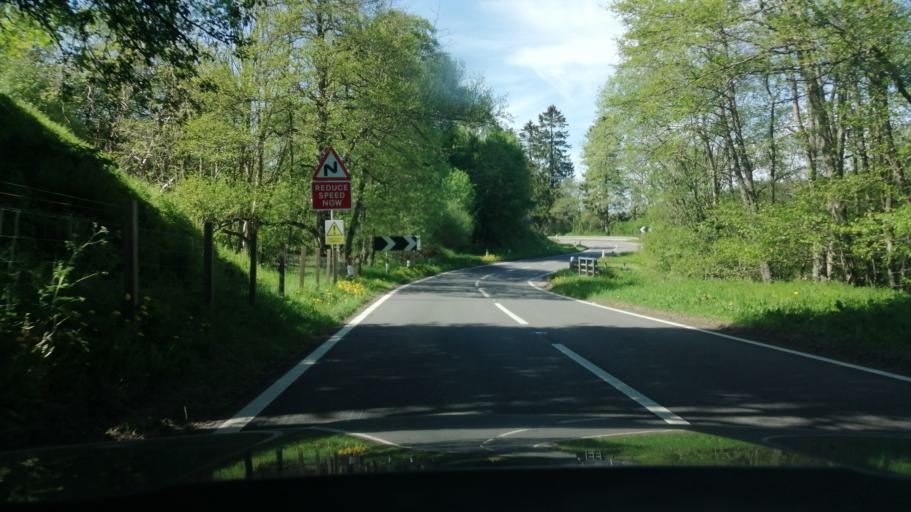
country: GB
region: Scotland
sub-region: Moray
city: Dufftown
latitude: 57.5027
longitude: -3.1313
